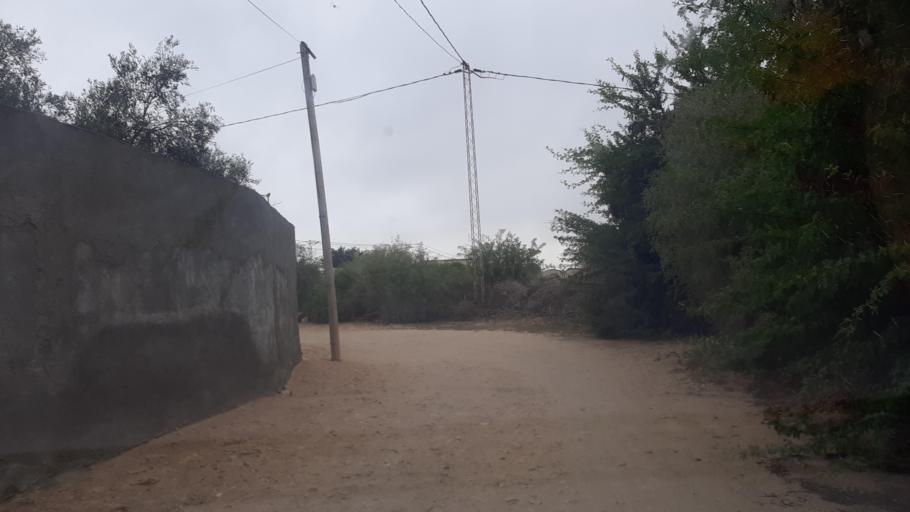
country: TN
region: Nabul
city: Menzel Heurr
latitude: 36.6839
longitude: 10.9279
